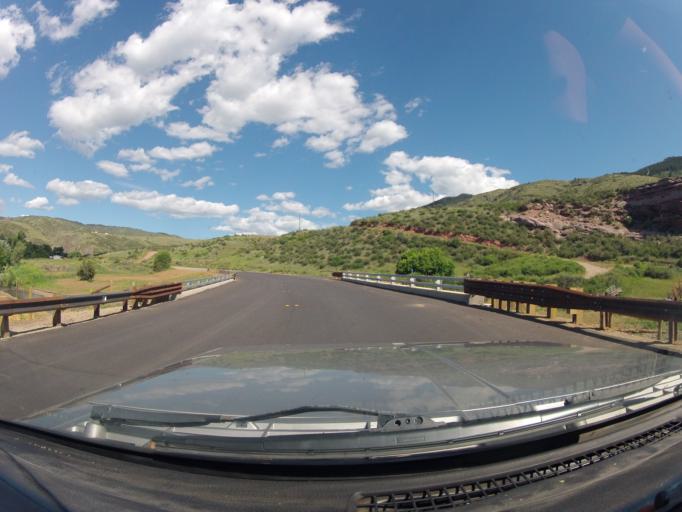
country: US
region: Colorado
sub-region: Larimer County
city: Laporte
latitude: 40.5205
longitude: -105.2516
